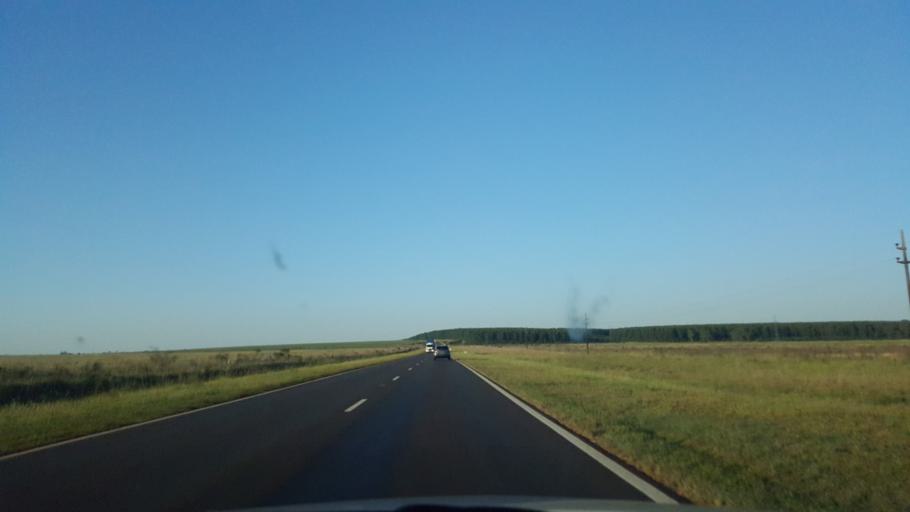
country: AR
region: Corrientes
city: Santo Tome
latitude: -28.4645
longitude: -56.1103
